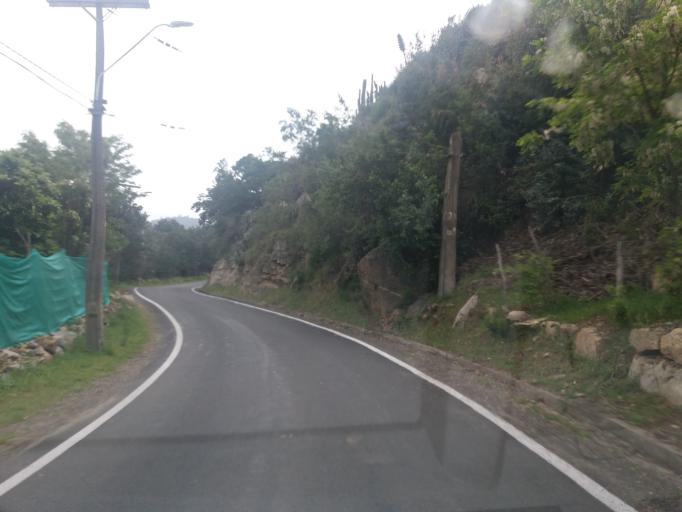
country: CL
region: Valparaiso
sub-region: Provincia de Marga Marga
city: Limache
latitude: -33.0325
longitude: -71.0847
